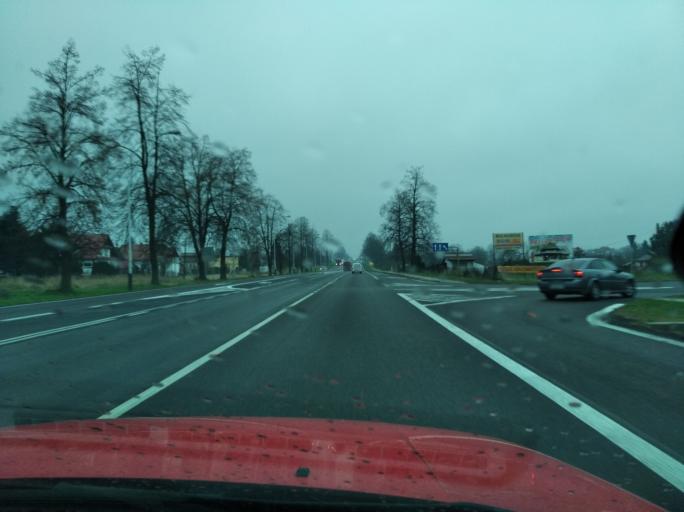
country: PL
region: Subcarpathian Voivodeship
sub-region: Powiat przeworski
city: Przeworsk
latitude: 50.0611
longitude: 22.4736
